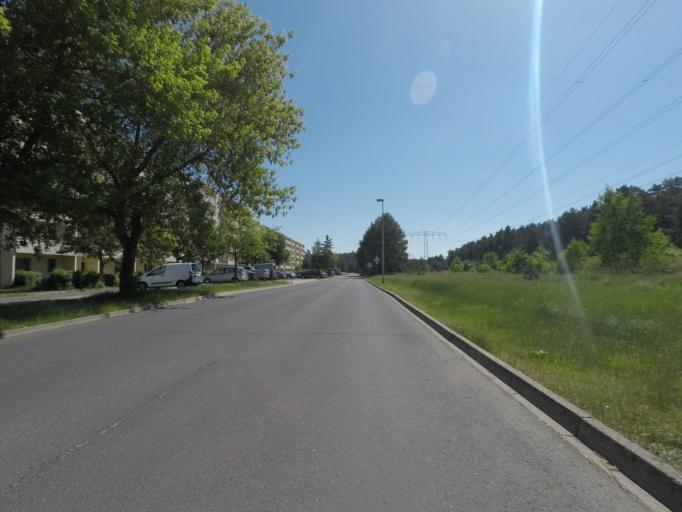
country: DE
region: Brandenburg
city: Eberswalde
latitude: 52.8318
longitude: 13.7518
